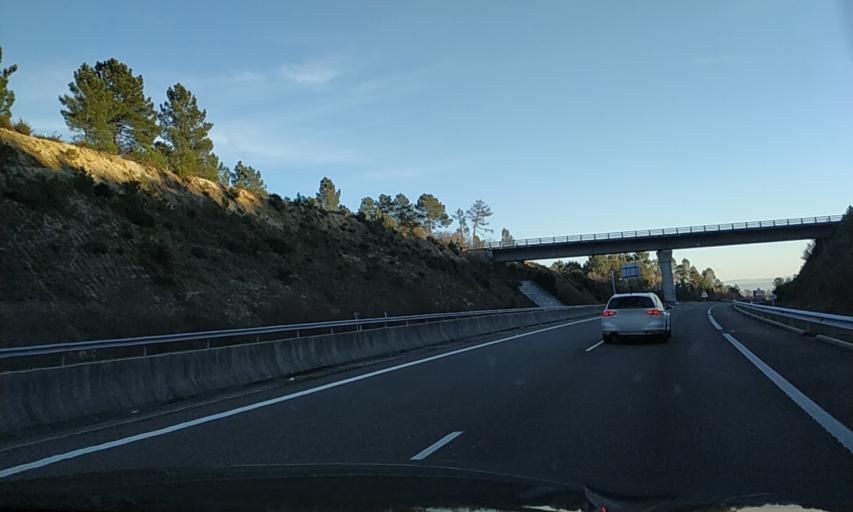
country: ES
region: Galicia
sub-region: Provincia de Ourense
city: Maside
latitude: 42.4432
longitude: -8.0184
